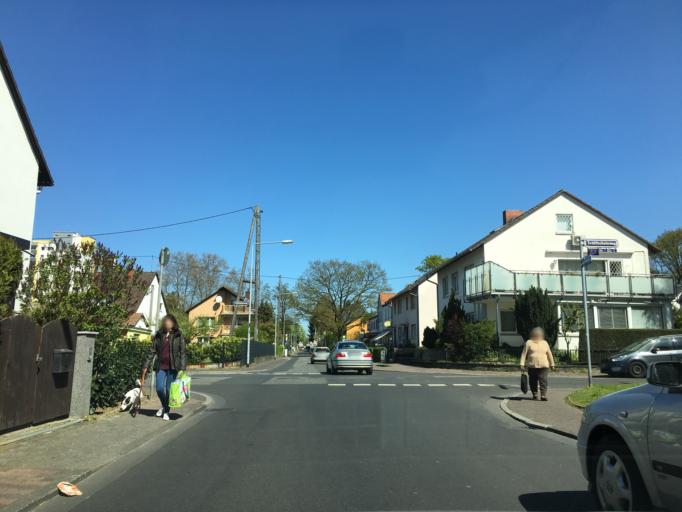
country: DE
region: Hesse
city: Niederrad
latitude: 50.0816
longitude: 8.6041
